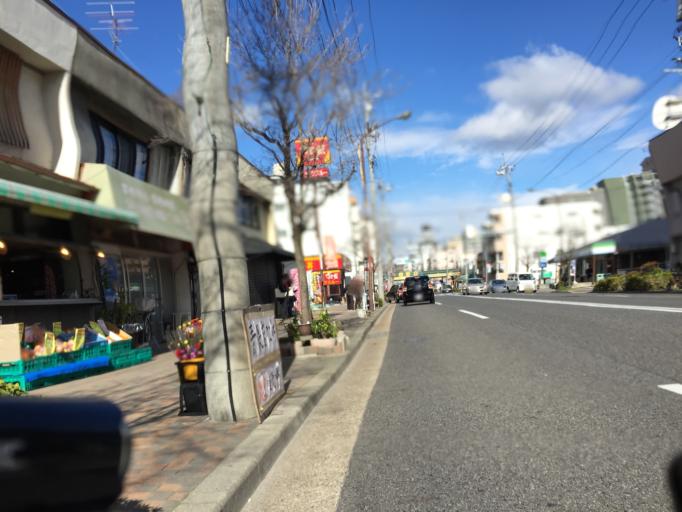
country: JP
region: Aichi
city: Nagoya-shi
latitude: 35.1646
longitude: 136.9274
